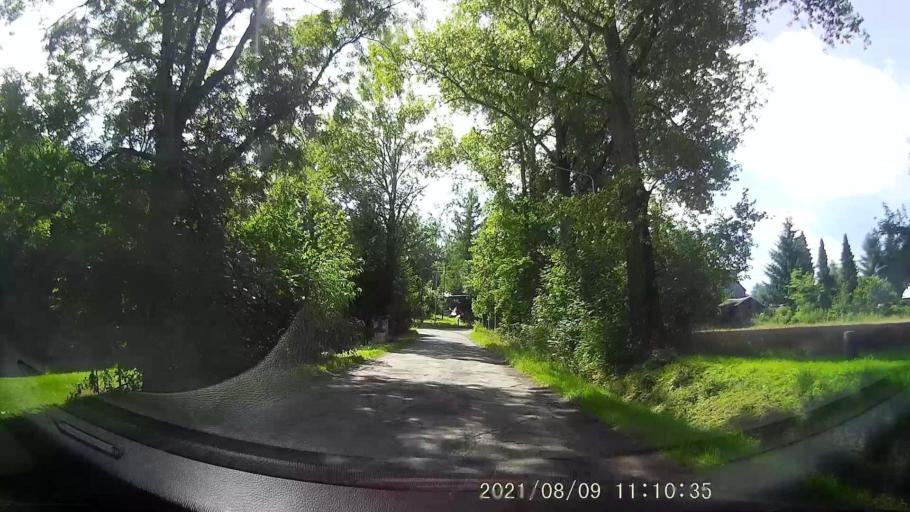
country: PL
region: Lower Silesian Voivodeship
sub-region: Powiat klodzki
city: Klodzko
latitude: 50.4478
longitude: 16.6257
